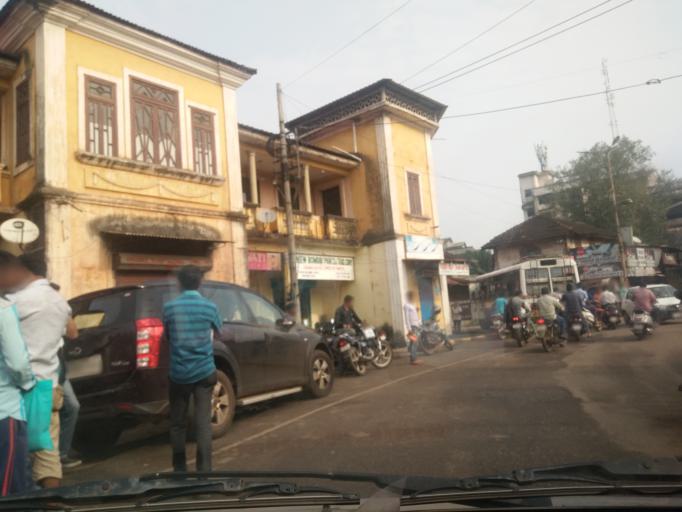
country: IN
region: Goa
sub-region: South Goa
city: Madgaon
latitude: 15.2689
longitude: 73.9586
